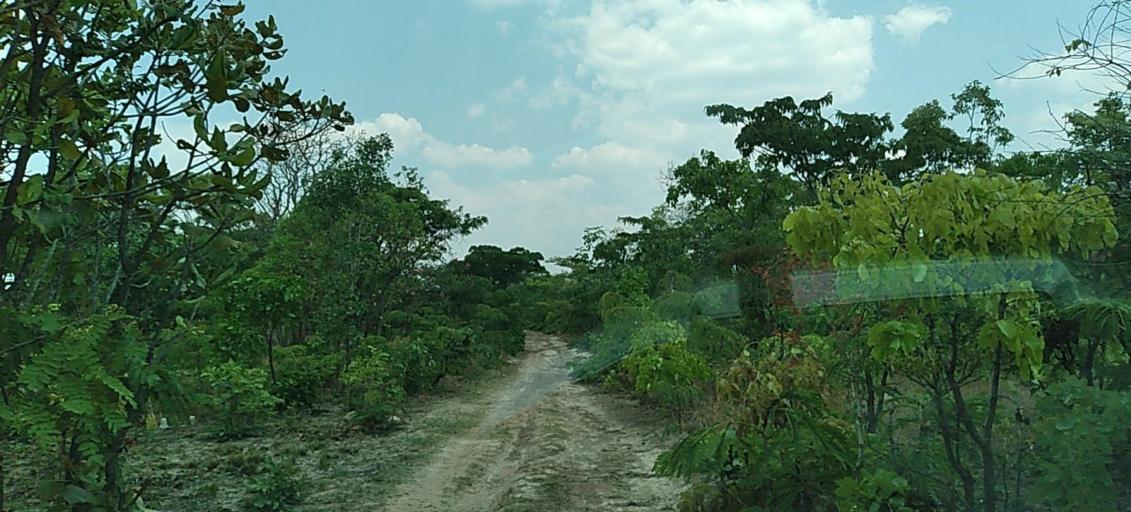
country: CD
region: Katanga
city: Kipushi
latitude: -12.0075
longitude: 27.4287
